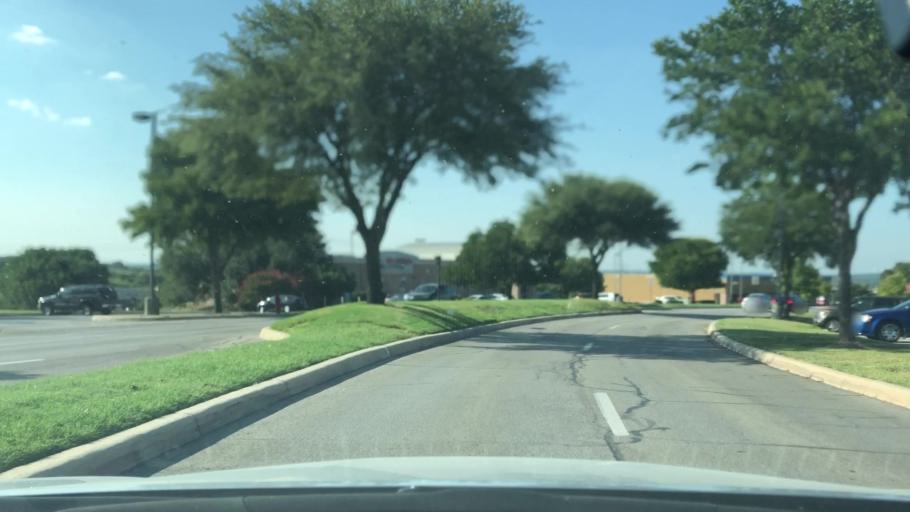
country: US
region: Texas
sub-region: Bexar County
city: Live Oak
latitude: 29.5733
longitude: -98.3243
